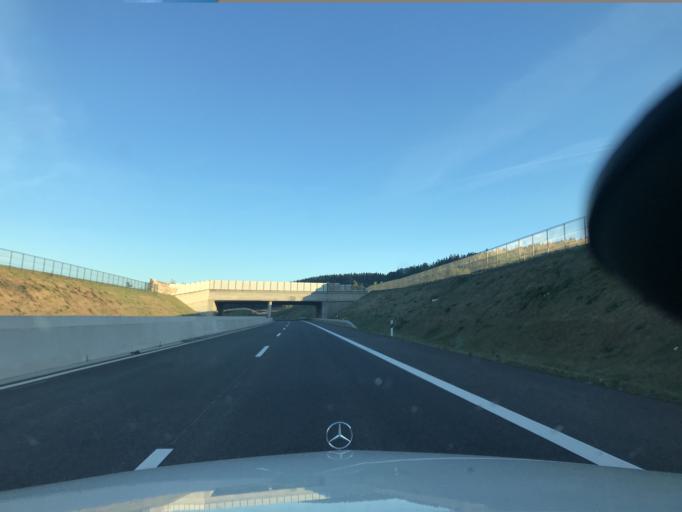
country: DE
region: Hesse
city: Waldkappel
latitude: 51.1602
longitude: 9.8521
